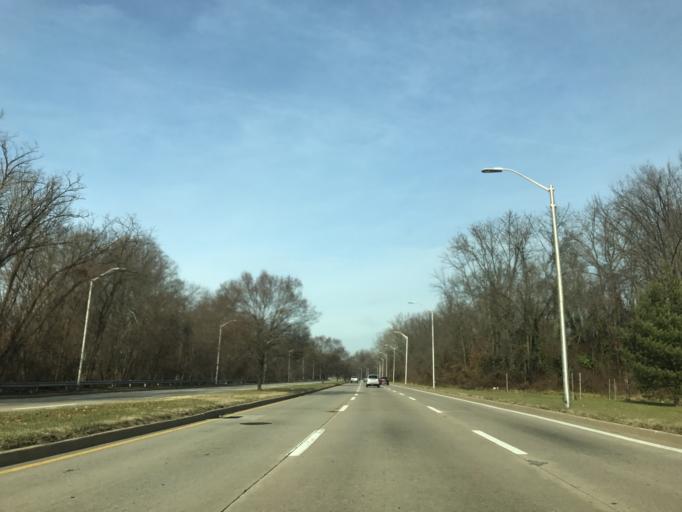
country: US
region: Maryland
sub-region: Baltimore County
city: Parkville
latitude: 39.3613
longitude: -76.5729
